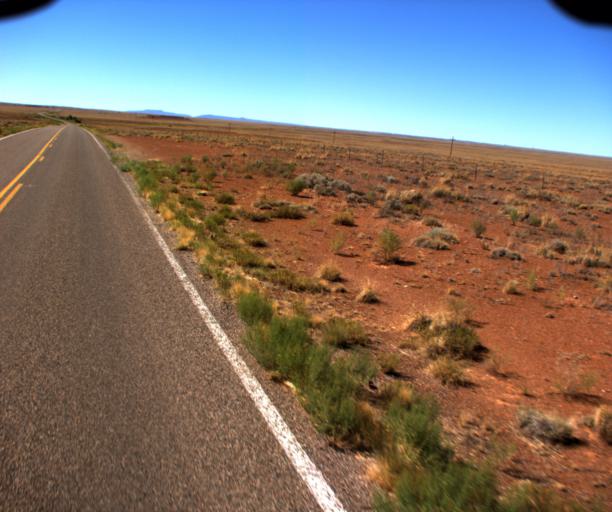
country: US
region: Arizona
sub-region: Coconino County
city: LeChee
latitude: 35.2387
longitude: -110.9597
